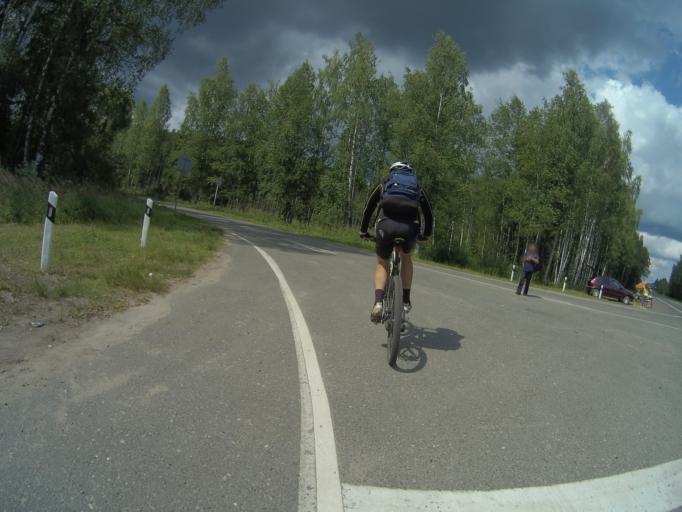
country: RU
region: Ivanovo
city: Novoye Leushino
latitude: 56.6492
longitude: 40.5829
